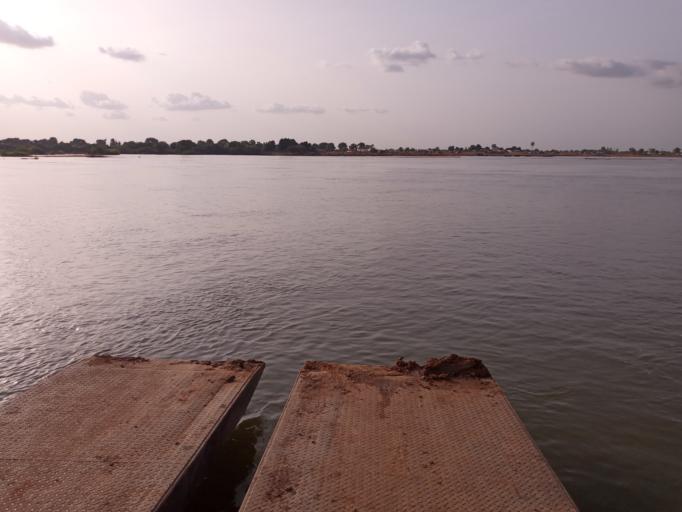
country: ML
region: Koulikoro
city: Kangaba
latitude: 12.1607
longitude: -8.2434
